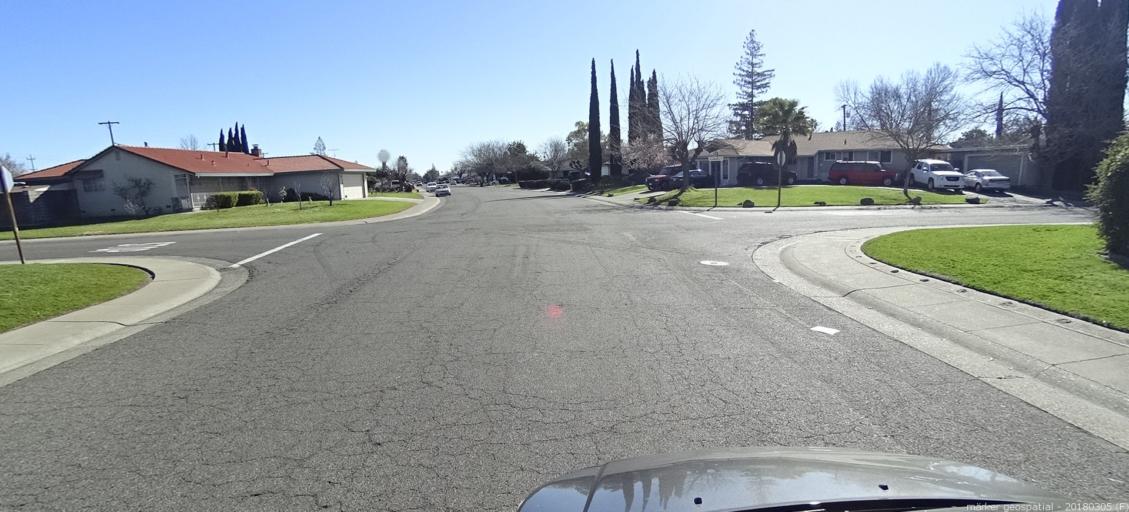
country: US
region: California
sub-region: Sacramento County
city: Florin
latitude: 38.4949
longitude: -121.4234
